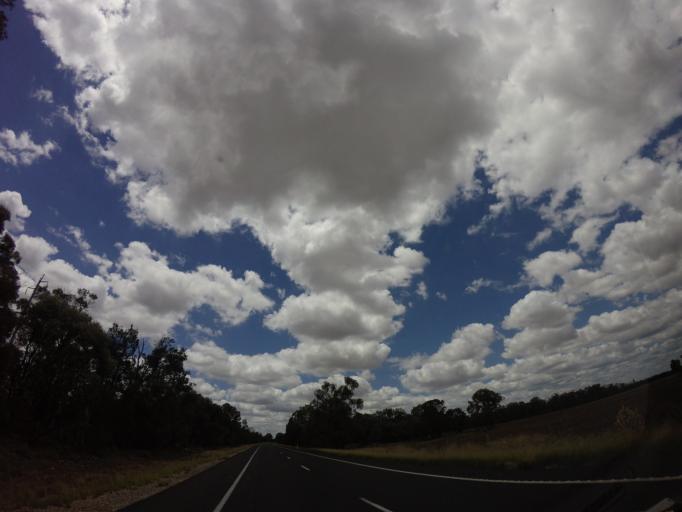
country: AU
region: Queensland
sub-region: Goondiwindi
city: Goondiwindi
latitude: -28.1249
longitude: 150.7046
